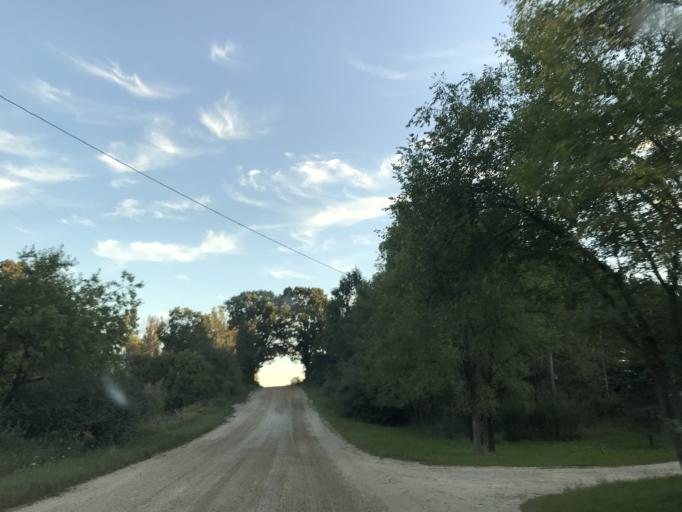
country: US
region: Michigan
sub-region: Mason County
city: Scottville
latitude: 43.9302
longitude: -86.1690
